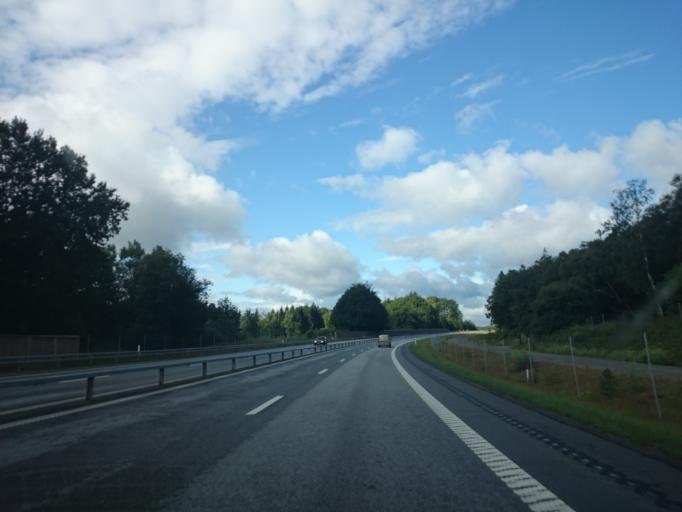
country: SE
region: Skane
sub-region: Horby Kommun
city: Hoerby
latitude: 55.9127
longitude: 13.7692
